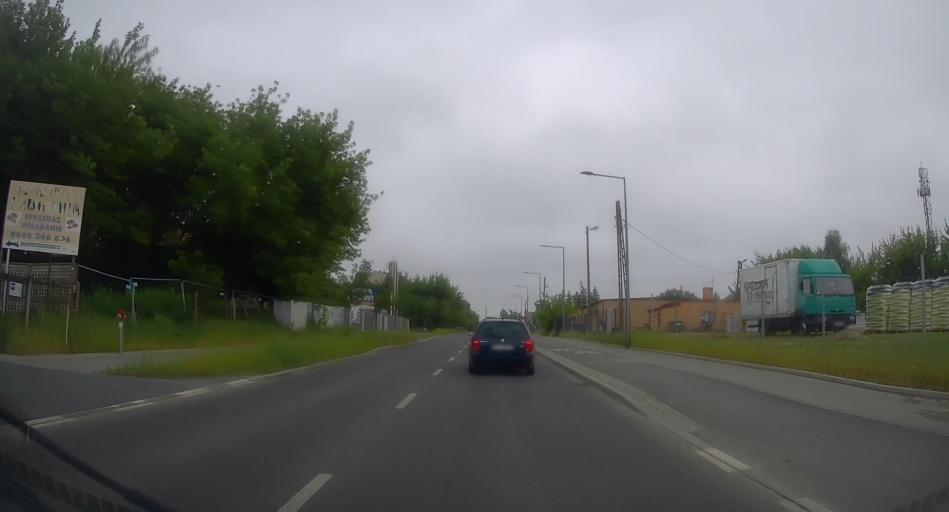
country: PL
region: Masovian Voivodeship
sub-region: Powiat piaseczynski
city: Piaseczno
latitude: 52.0715
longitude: 21.0162
